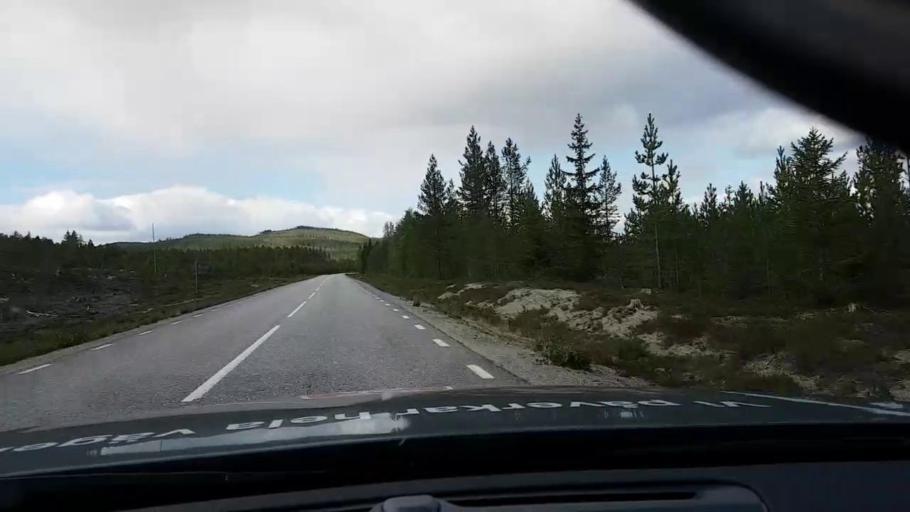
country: SE
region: Vaesternorrland
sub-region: OErnskoeldsviks Kommun
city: Bredbyn
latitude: 63.6785
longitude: 17.7901
